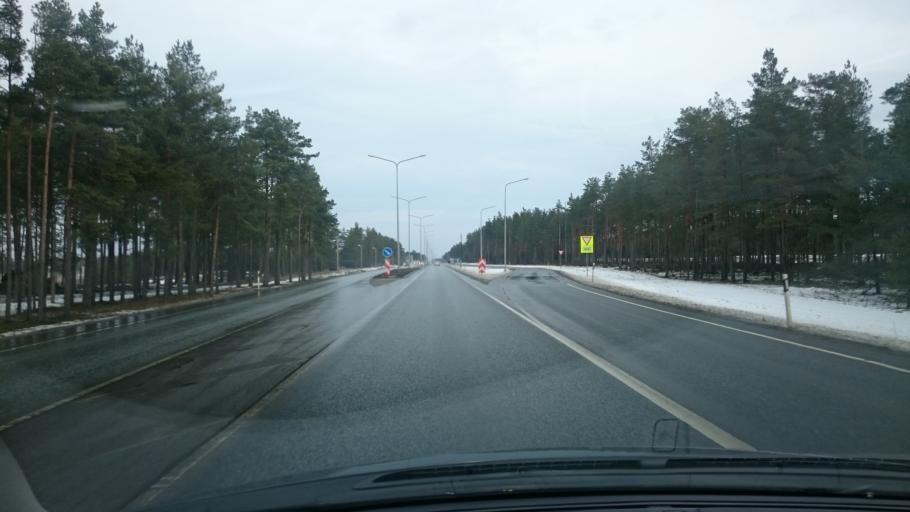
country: EE
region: Harju
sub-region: Saku vald
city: Saku
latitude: 59.3310
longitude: 24.6950
